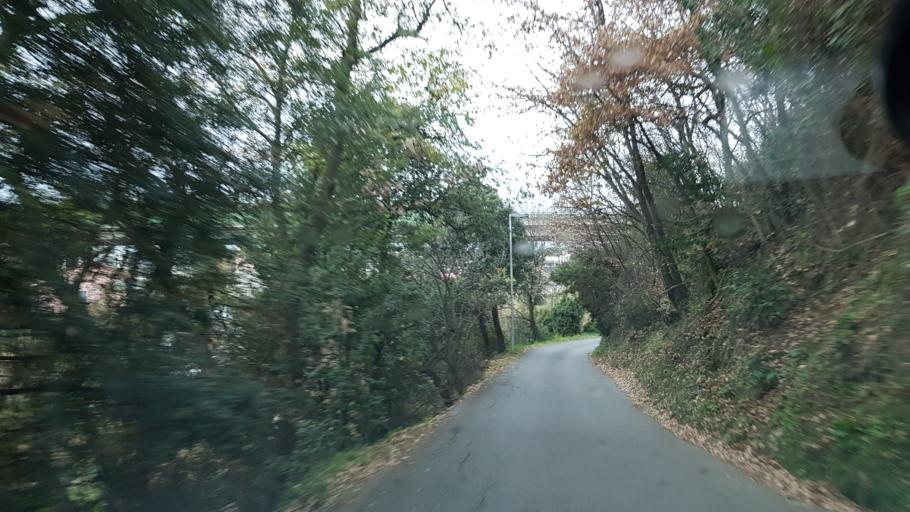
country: IT
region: Liguria
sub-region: Provincia di Savona
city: Savona
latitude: 44.3037
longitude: 8.4484
